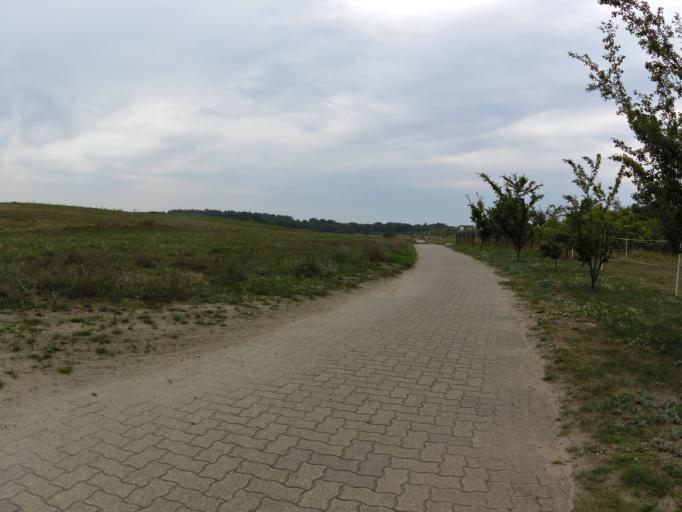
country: DE
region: Mecklenburg-Vorpommern
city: Seebad Heringsdorf
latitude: 53.8788
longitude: 14.1708
